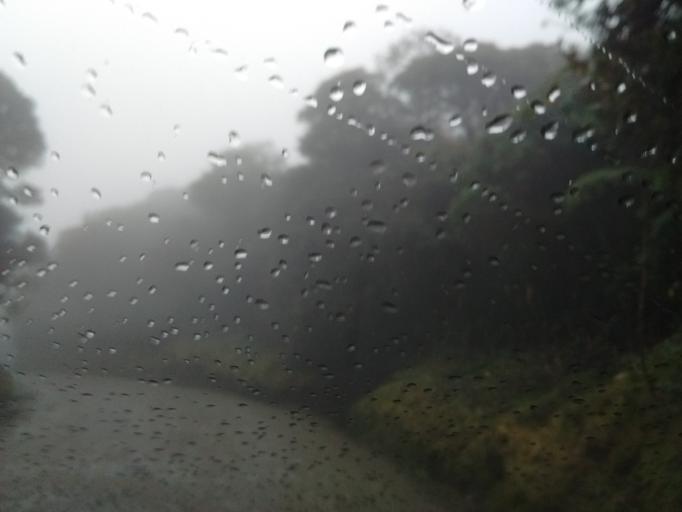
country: CO
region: Cauca
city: Paispamba
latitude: 2.1604
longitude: -76.4218
